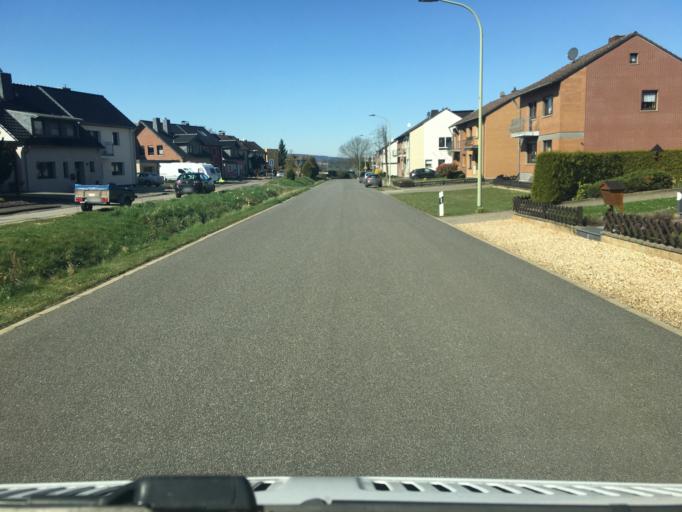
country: DE
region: North Rhine-Westphalia
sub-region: Regierungsbezirk Koln
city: Kreuzau
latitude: 50.7331
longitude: 6.5184
